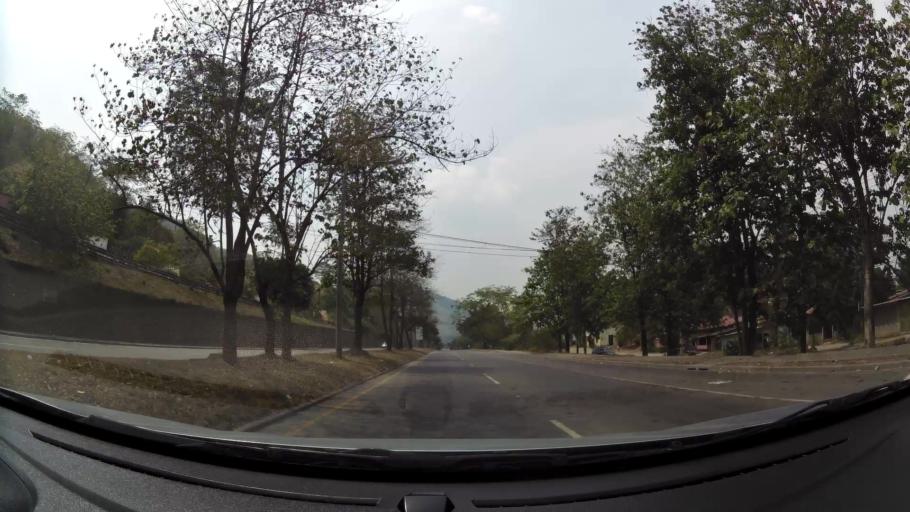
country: HN
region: Cortes
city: Chotepe
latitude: 15.4167
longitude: -88.0162
